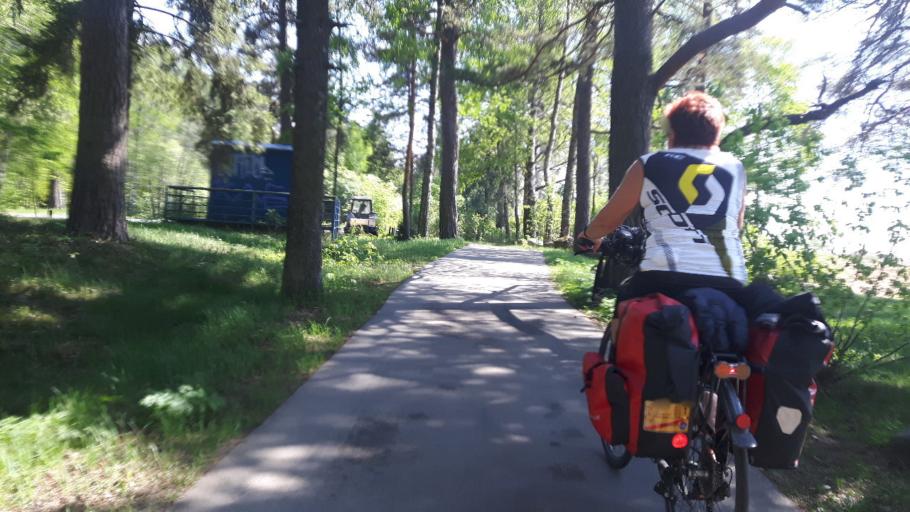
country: RU
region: St.-Petersburg
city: Komarovo
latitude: 60.1766
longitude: 29.7945
